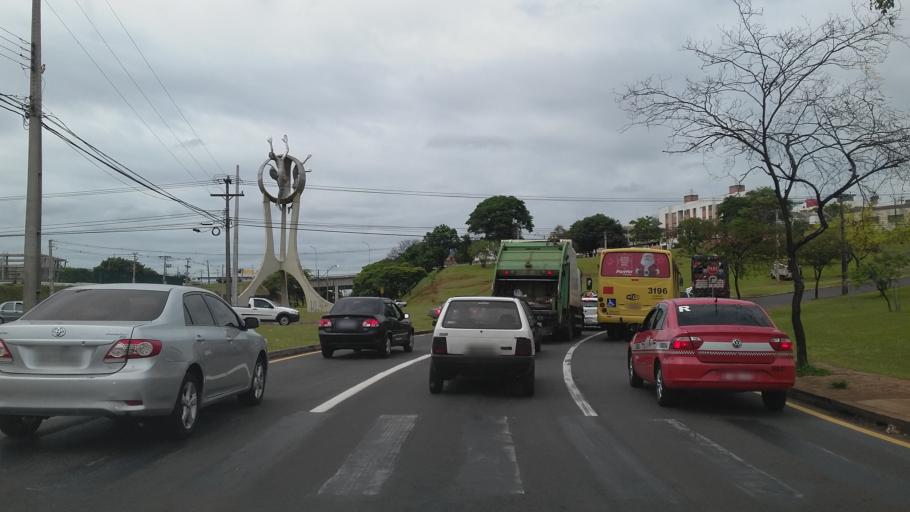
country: BR
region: Parana
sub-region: Londrina
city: Londrina
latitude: -23.3107
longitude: -51.1490
